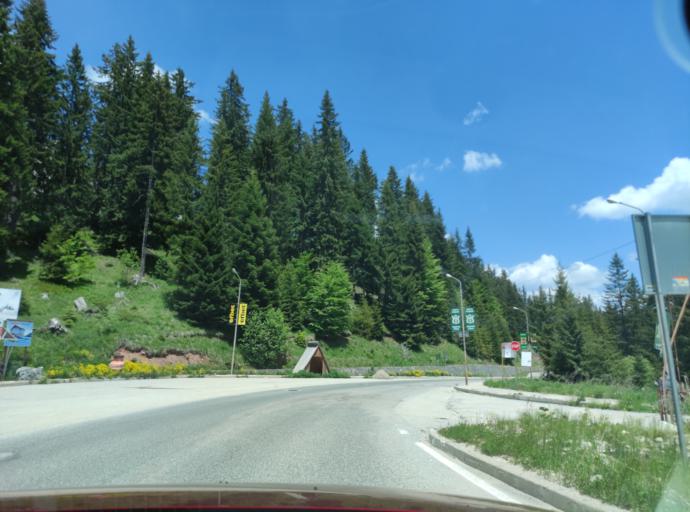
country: BG
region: Smolyan
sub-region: Obshtina Smolyan
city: Smolyan
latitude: 41.6417
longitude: 24.6912
